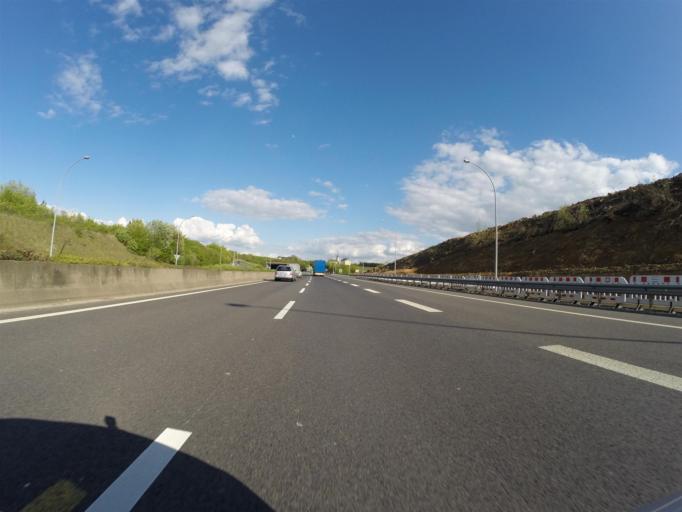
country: LU
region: Luxembourg
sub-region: Canton d'Esch-sur-Alzette
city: Frisange
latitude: 49.5083
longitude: 6.1862
